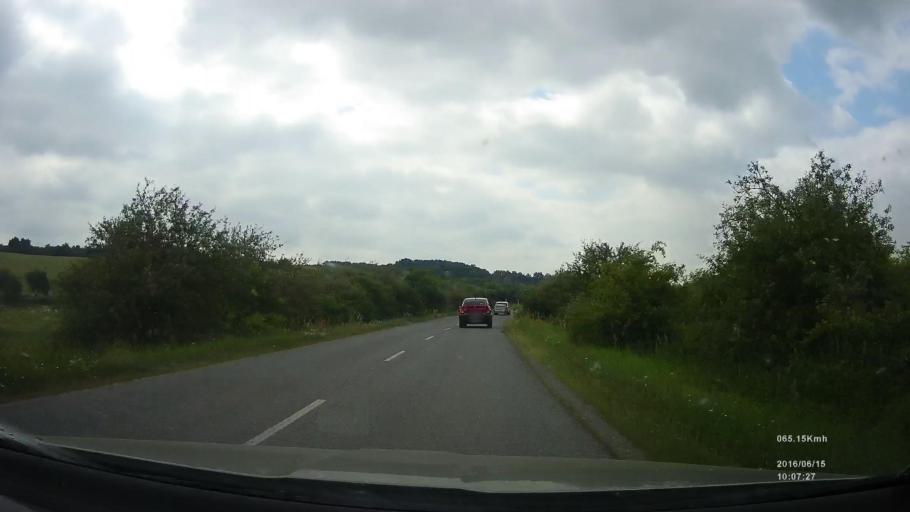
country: SK
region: Kosicky
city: Kosice
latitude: 48.7770
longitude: 21.3295
